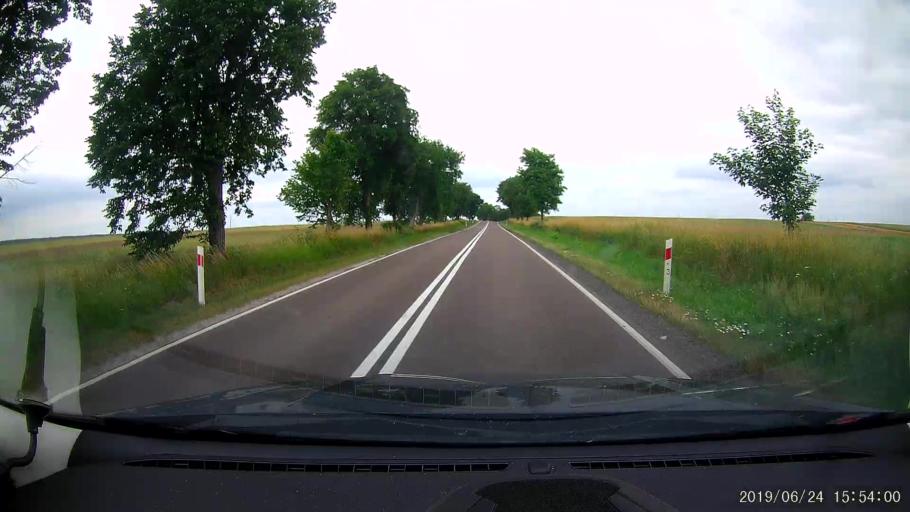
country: PL
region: Subcarpathian Voivodeship
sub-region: Powiat lubaczowski
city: Cieszanow
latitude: 50.2122
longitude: 23.1118
